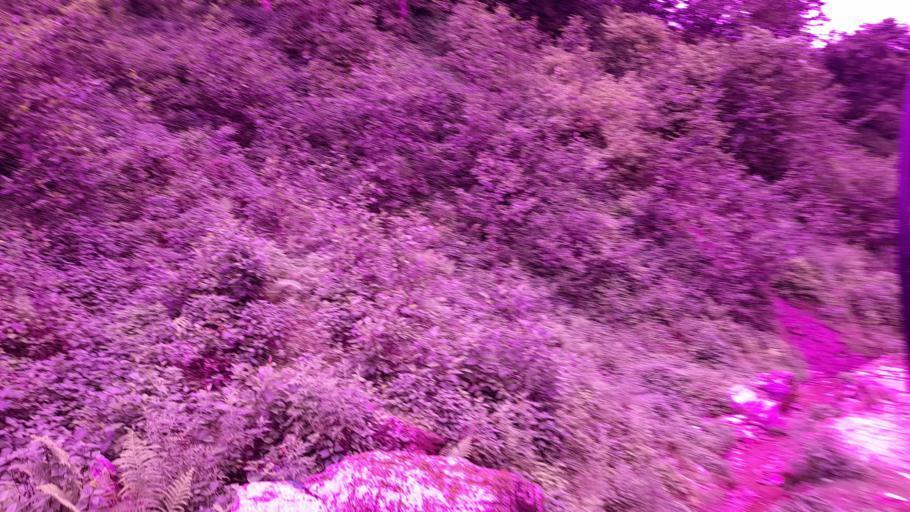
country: NP
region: Central Region
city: Kirtipur
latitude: 27.8243
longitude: 85.2101
